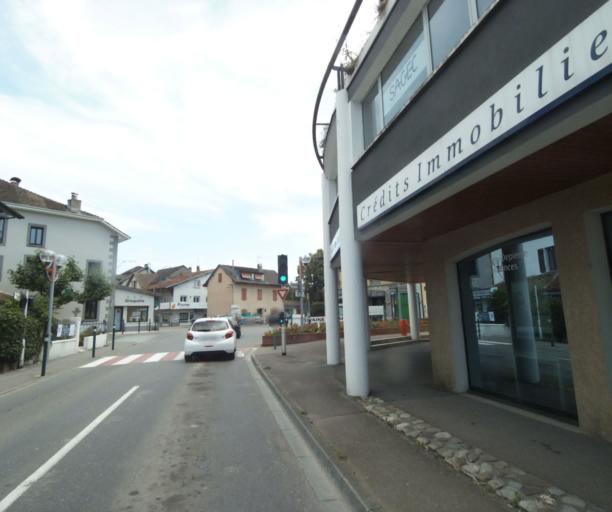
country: FR
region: Rhone-Alpes
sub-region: Departement de la Haute-Savoie
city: Douvaine
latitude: 46.3058
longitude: 6.3008
